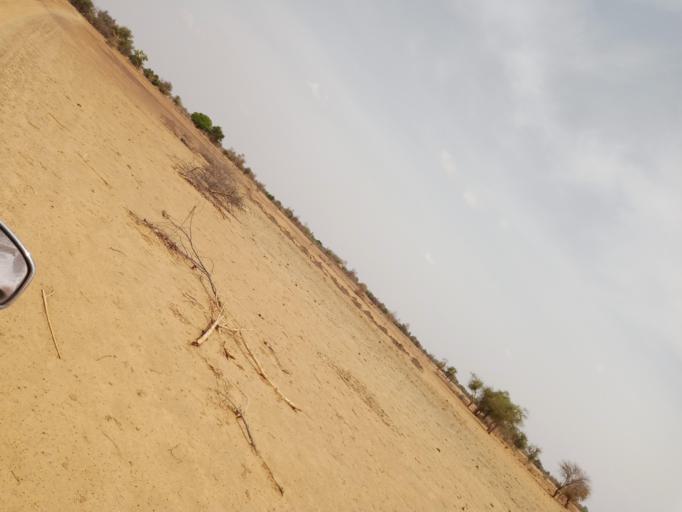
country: BF
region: Est
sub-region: Gnagna Province
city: Bogande
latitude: 13.0947
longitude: -0.0361
